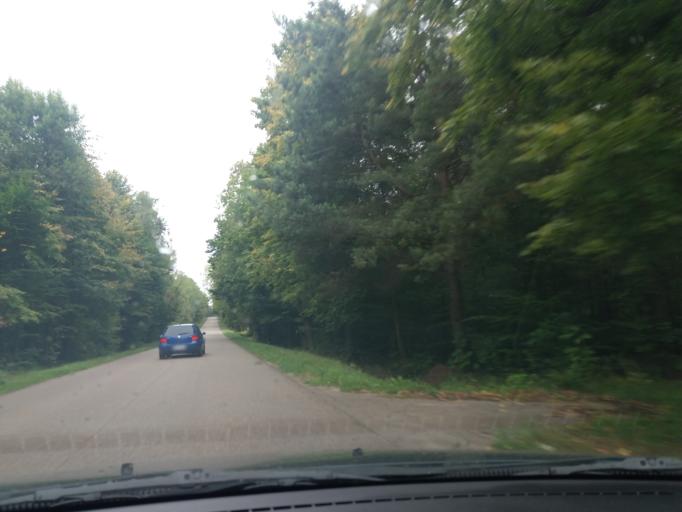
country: PL
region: Masovian Voivodeship
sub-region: Powiat mlawski
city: Wieczfnia Koscielna
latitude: 53.2118
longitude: 20.5045
